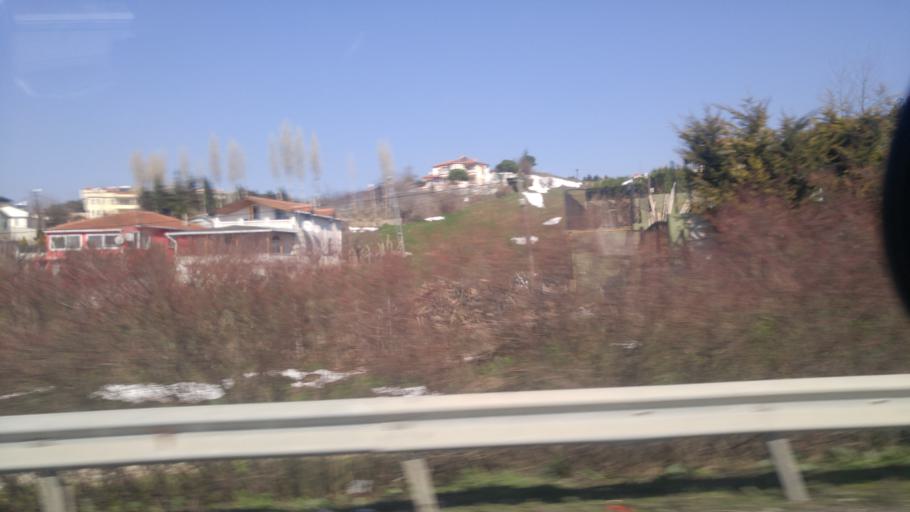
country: TR
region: Istanbul
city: Celaliye
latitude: 41.0580
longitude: 28.4158
